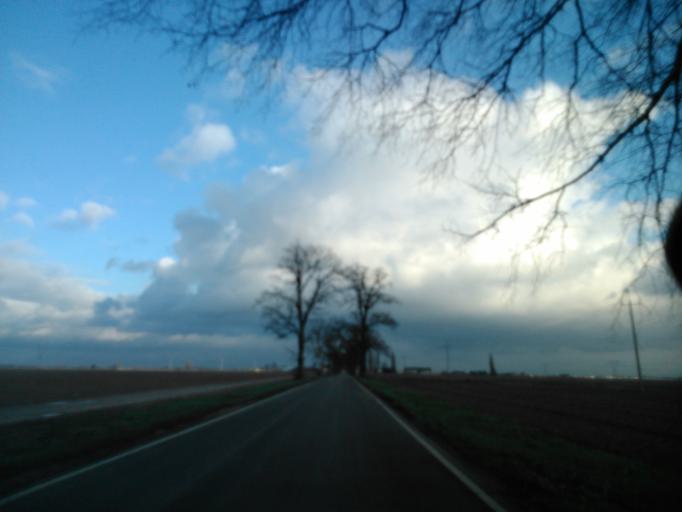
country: PL
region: Masovian Voivodeship
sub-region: Powiat warszawski zachodni
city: Leszno
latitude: 52.2431
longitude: 20.6108
